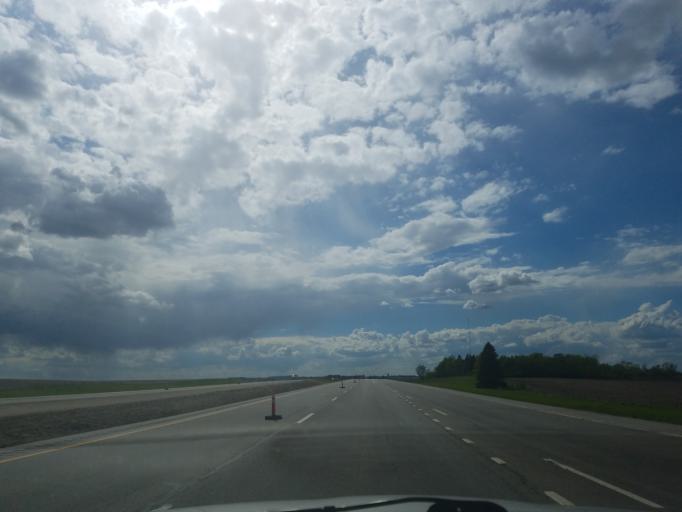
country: US
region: North Dakota
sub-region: Barnes County
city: Valley City
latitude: 46.9202
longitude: -97.7932
